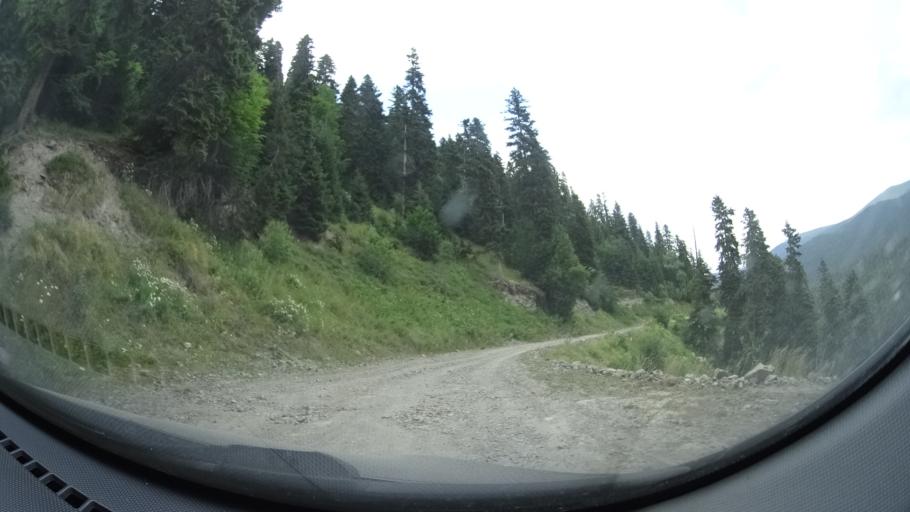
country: GE
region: Samtskhe-Javakheti
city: Adigeni
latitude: 41.6370
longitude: 42.5796
